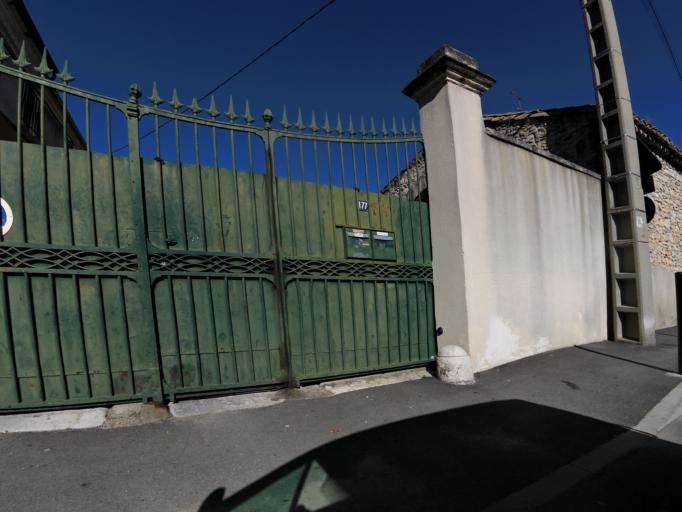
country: FR
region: Languedoc-Roussillon
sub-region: Departement du Gard
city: Nimes
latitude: 43.8283
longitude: 4.3636
